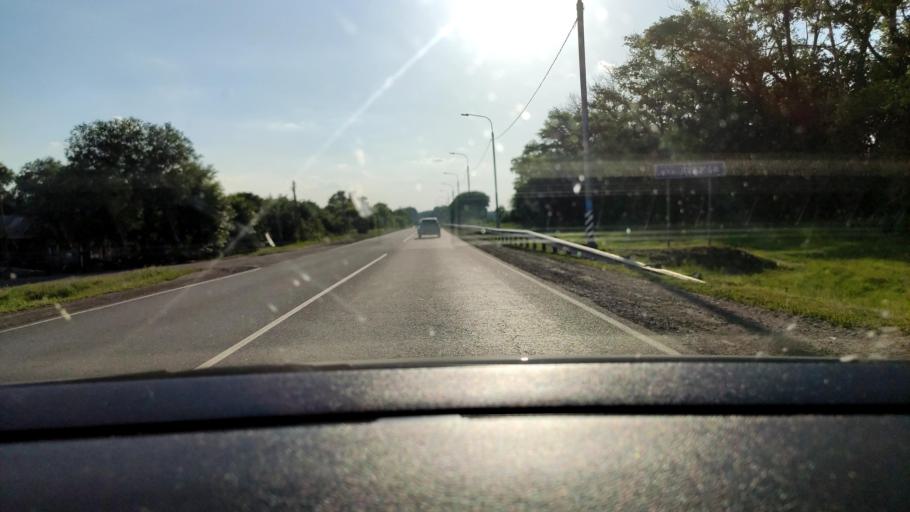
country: RU
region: Voronezj
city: Kashirskoye
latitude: 51.4581
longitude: 39.8116
